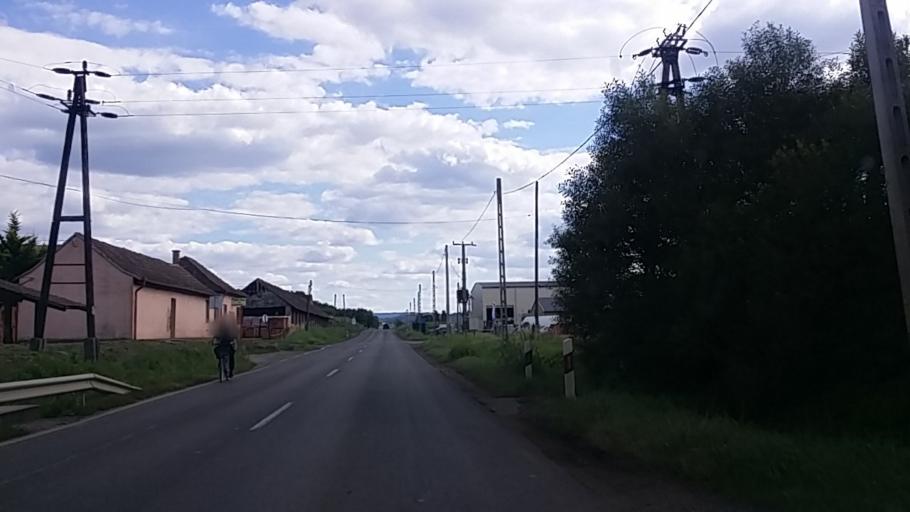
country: HU
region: Baranya
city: Sasd
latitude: 46.2448
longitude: 18.1207
